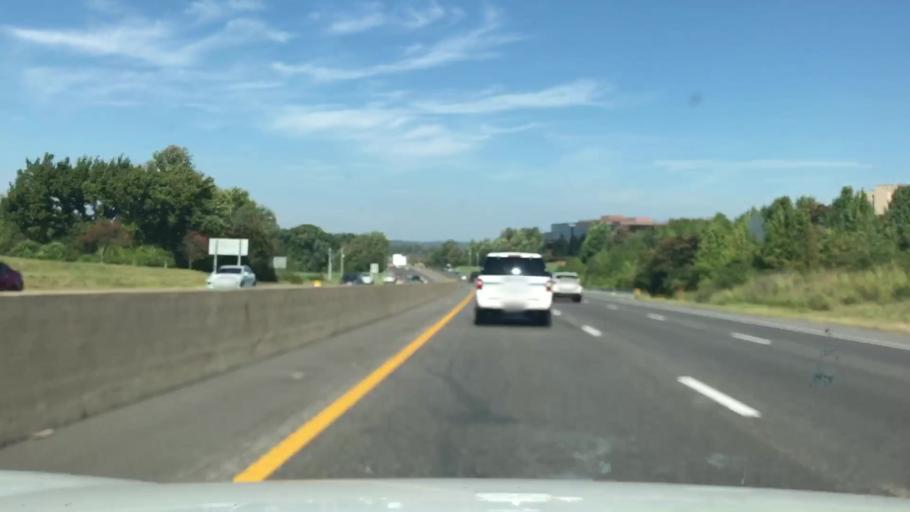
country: US
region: Missouri
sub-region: Saint Louis County
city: Chesterfield
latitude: 38.6595
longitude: -90.5673
